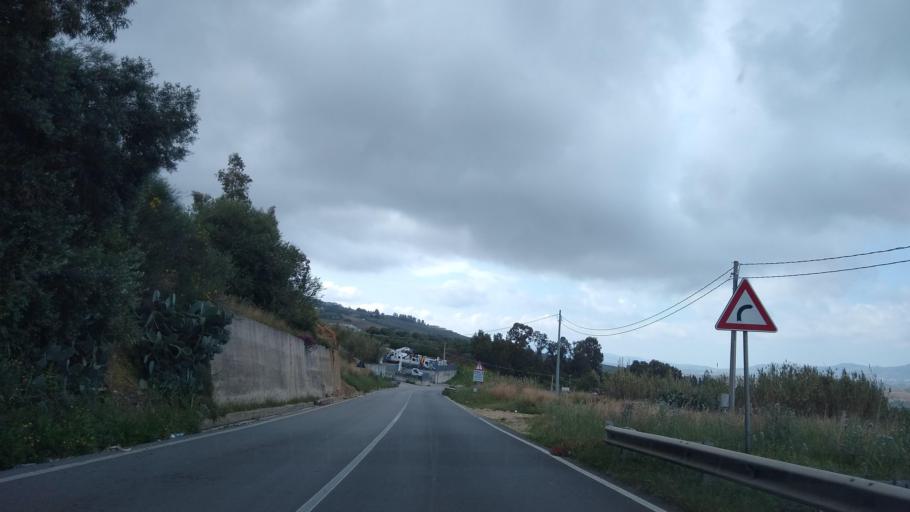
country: IT
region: Sicily
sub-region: Trapani
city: Alcamo
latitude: 37.9761
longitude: 12.9355
